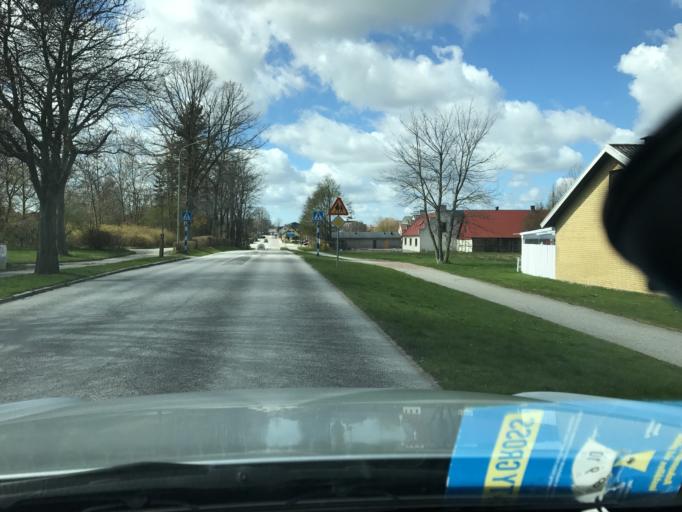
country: SE
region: Skane
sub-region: Skurups Kommun
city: Skurup
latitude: 55.4821
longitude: 13.5078
